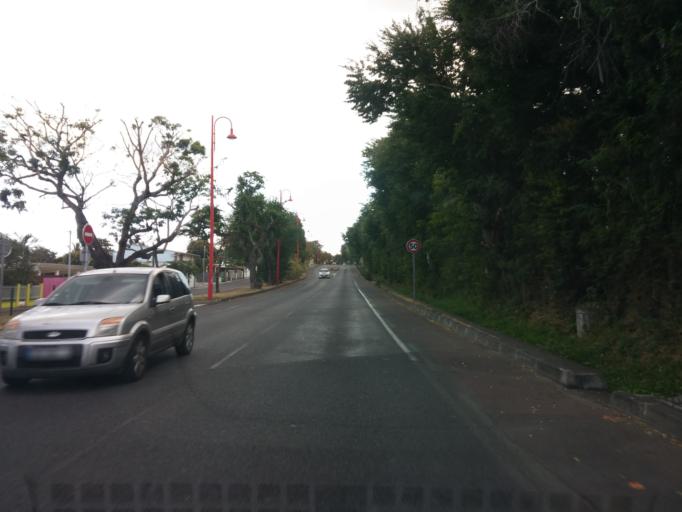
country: RE
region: Reunion
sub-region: Reunion
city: La Possession
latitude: -20.9386
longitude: 55.3318
